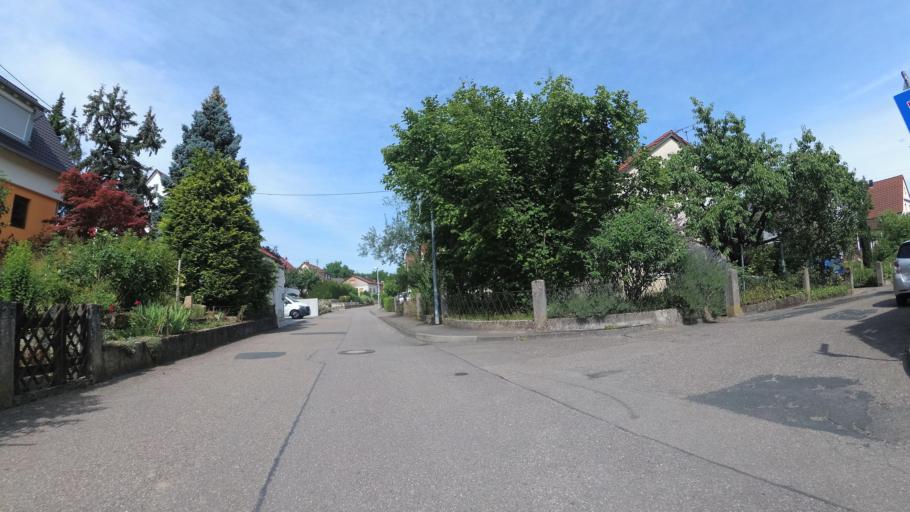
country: DE
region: Baden-Wuerttemberg
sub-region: Regierungsbezirk Stuttgart
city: Eberstadt
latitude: 49.1816
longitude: 9.2990
